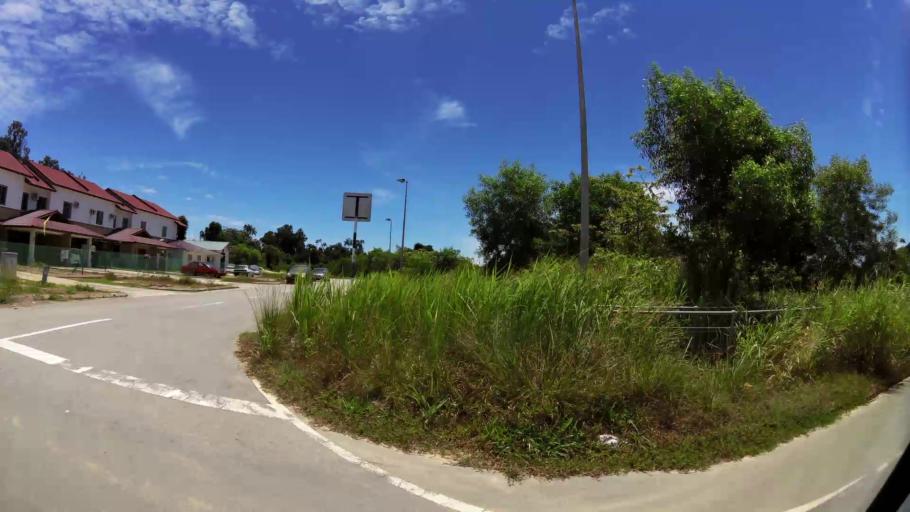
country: BN
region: Brunei and Muara
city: Bandar Seri Begawan
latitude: 5.0108
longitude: 115.0233
